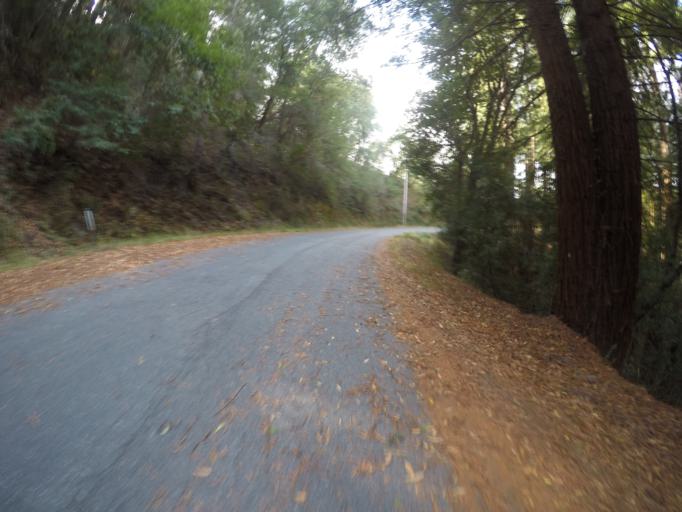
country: US
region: California
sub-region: Santa Cruz County
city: Scotts Valley
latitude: 37.0521
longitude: -121.9643
